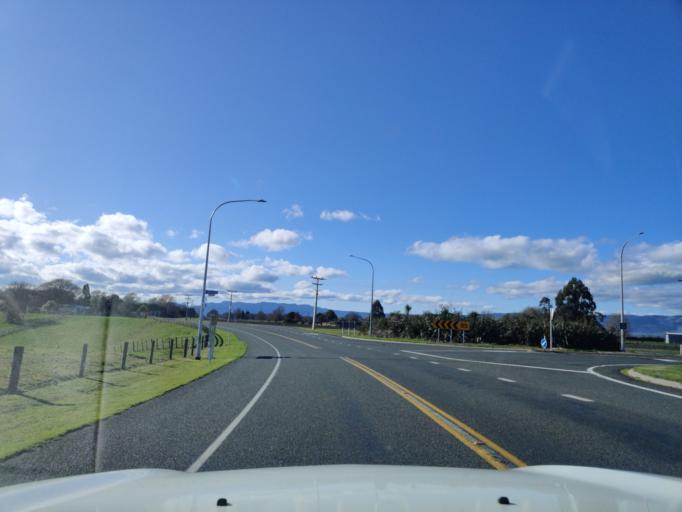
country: NZ
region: Waikato
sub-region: Matamata-Piako District
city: Matamata
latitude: -37.8639
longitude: 175.7538
